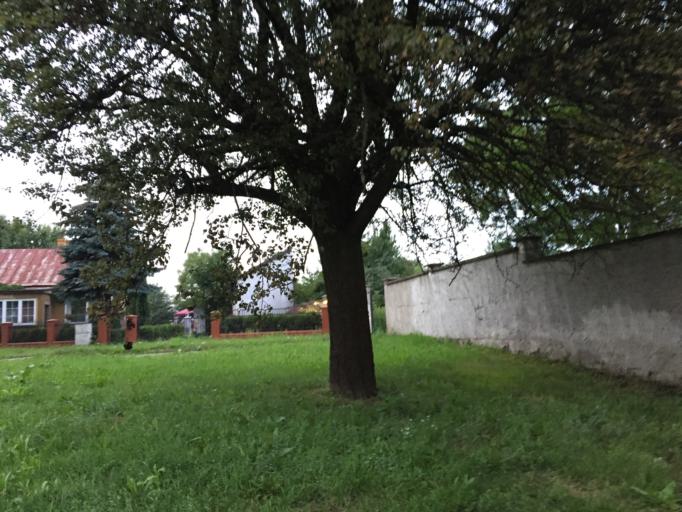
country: PL
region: Podlasie
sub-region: Bialystok
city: Bialystok
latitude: 53.1407
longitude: 23.1036
